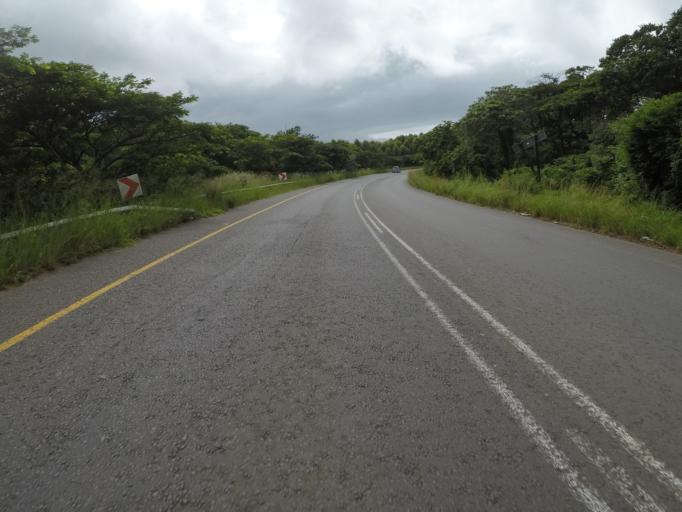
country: ZA
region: KwaZulu-Natal
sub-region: uThungulu District Municipality
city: eSikhawini
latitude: -28.8642
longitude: 31.8931
